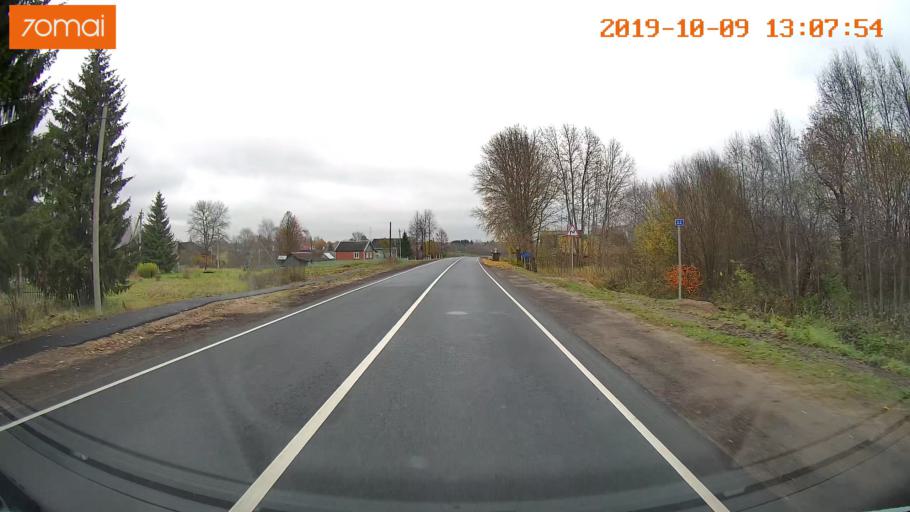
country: RU
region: Jaroslavl
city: Lyubim
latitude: 58.3564
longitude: 40.6546
